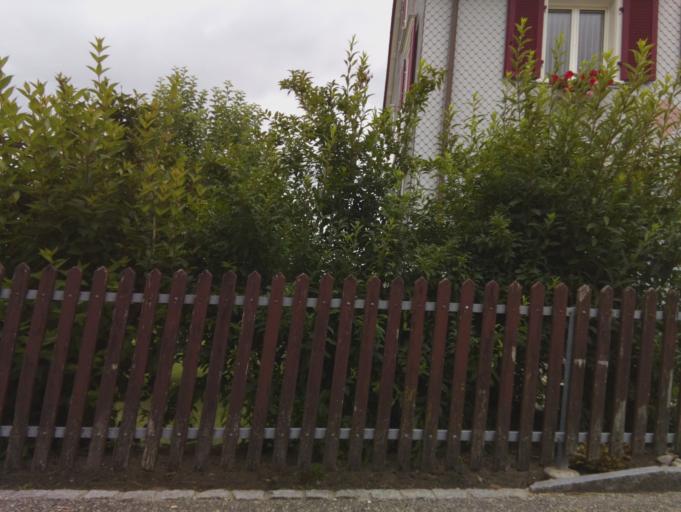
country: CH
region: Saint Gallen
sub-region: Wahlkreis Toggenburg
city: Ganterschwil
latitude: 47.3816
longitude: 9.0907
